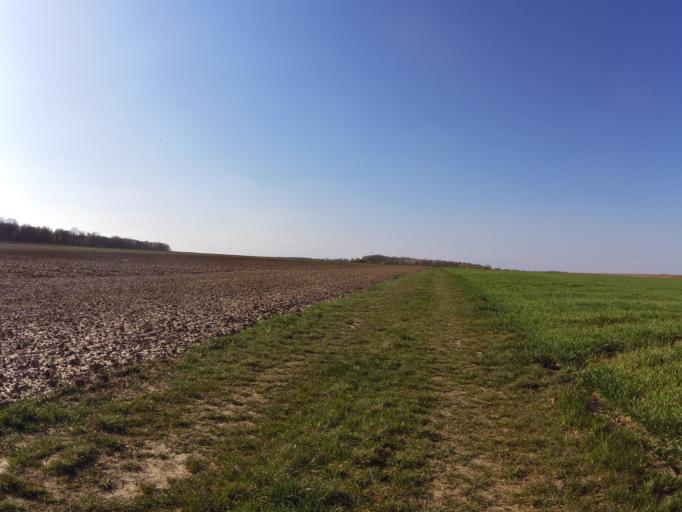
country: DE
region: Bavaria
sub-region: Regierungsbezirk Unterfranken
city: Oberpleichfeld
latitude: 49.8319
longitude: 10.0805
